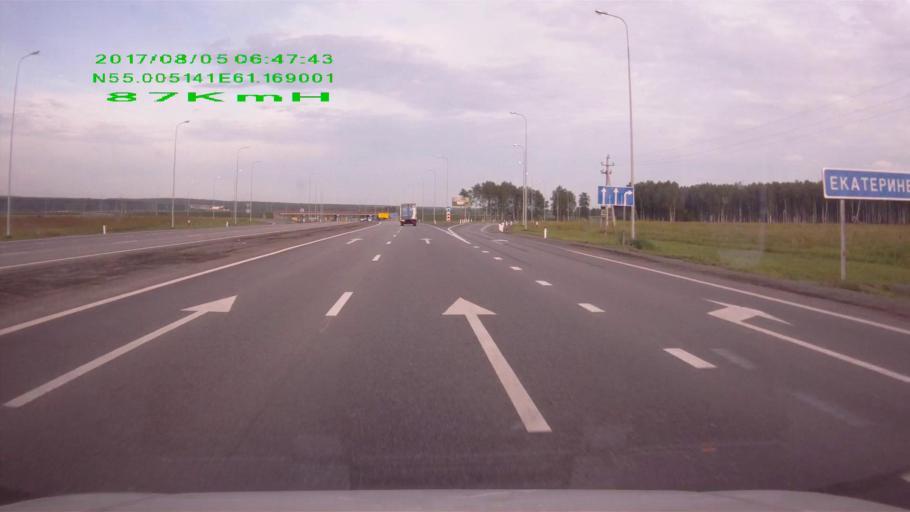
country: RU
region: Chelyabinsk
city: Poletayevo
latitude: 55.0051
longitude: 61.1688
